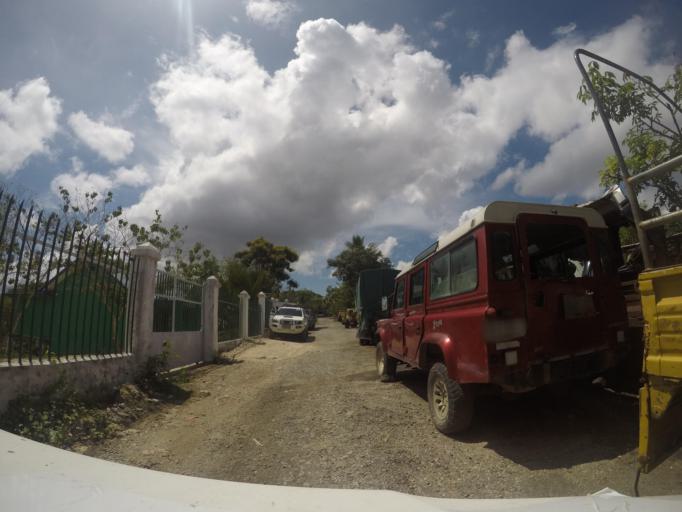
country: TL
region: Baucau
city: Baucau
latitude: -8.4726
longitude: 126.4570
